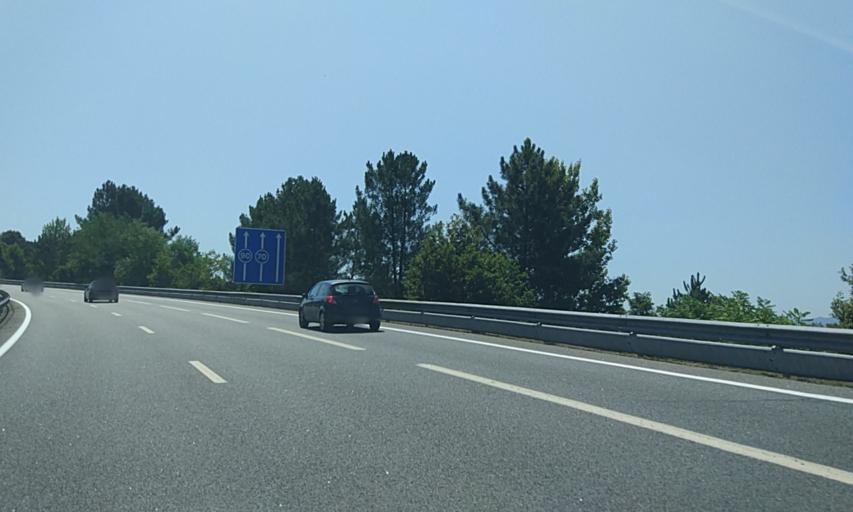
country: PT
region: Porto
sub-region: Amarante
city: Figueiro
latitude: 41.2439
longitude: -8.1712
